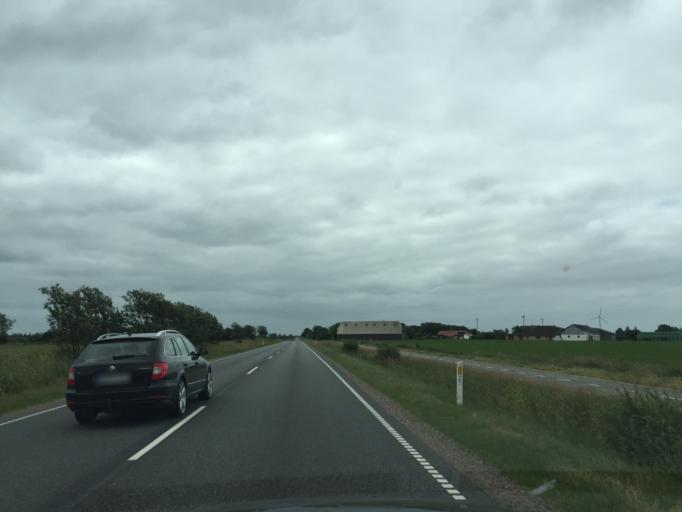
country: DK
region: South Denmark
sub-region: Tonder Kommune
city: Sherrebek
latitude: 55.2266
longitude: 8.7248
